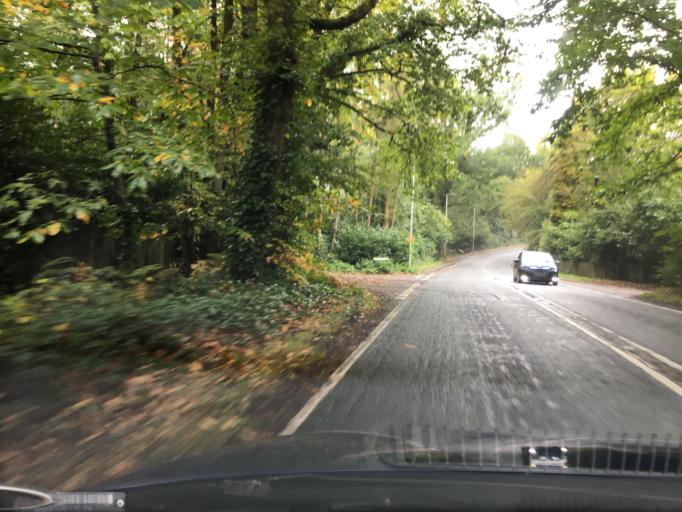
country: GB
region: England
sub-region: Hampshire
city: Yateley
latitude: 51.3594
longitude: -0.8183
